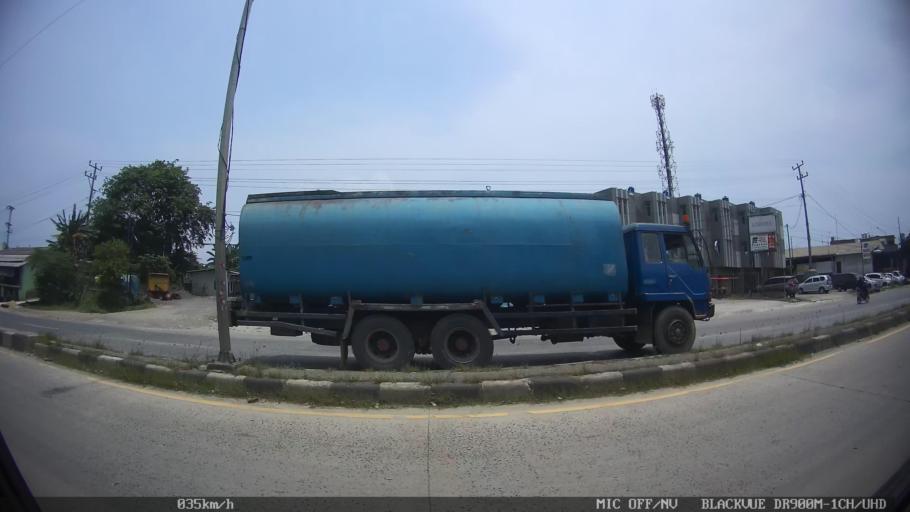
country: ID
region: Lampung
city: Kedaton
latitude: -5.3994
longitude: 105.2901
